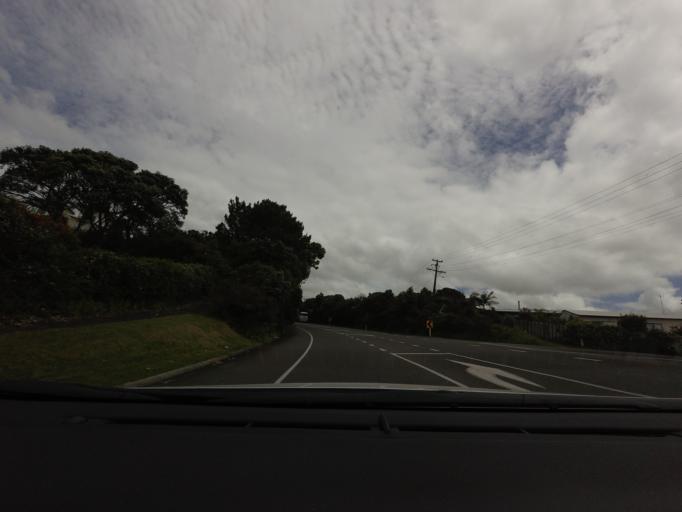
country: NZ
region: Auckland
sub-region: Auckland
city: Rothesay Bay
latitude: -36.5688
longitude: 174.6916
